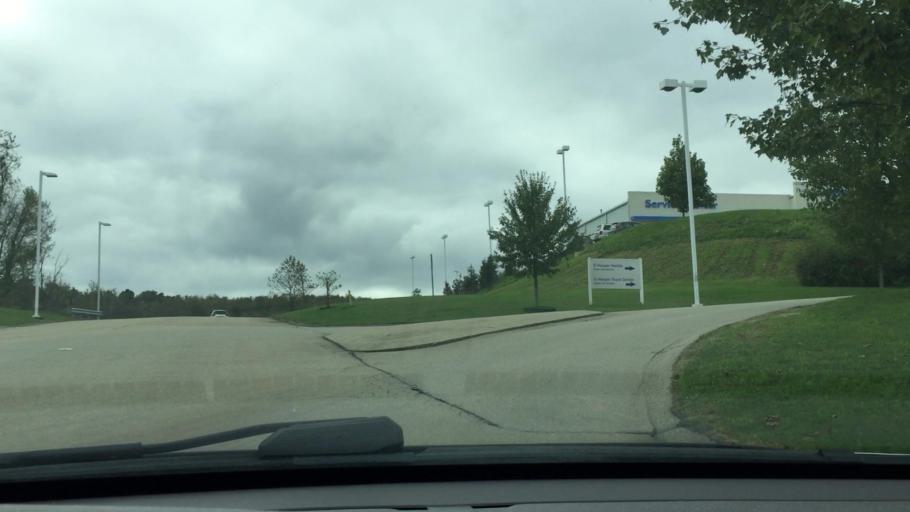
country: US
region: Pennsylvania
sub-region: Westmoreland County
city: Fellsburg
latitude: 40.1620
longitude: -79.7846
